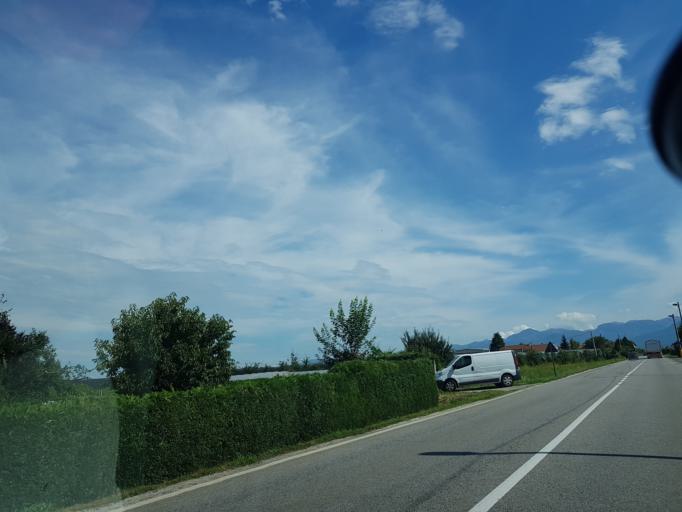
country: IT
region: Piedmont
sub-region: Provincia di Cuneo
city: Roata Rossi
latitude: 44.4409
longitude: 7.5320
